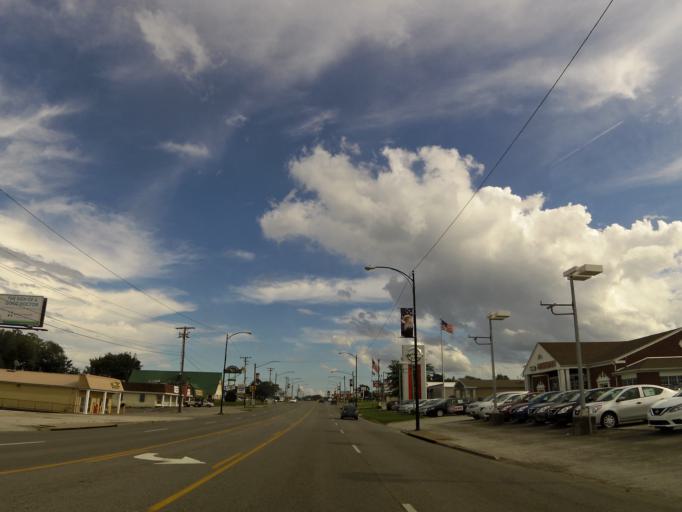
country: US
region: Kentucky
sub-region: Christian County
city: Hopkinsville
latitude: 36.8472
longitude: -87.4860
